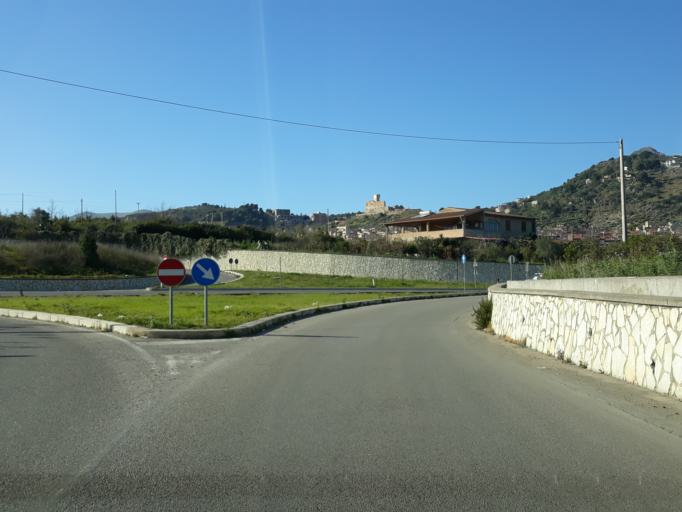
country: IT
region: Sicily
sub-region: Palermo
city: Misilmeri
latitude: 38.0282
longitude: 13.4560
